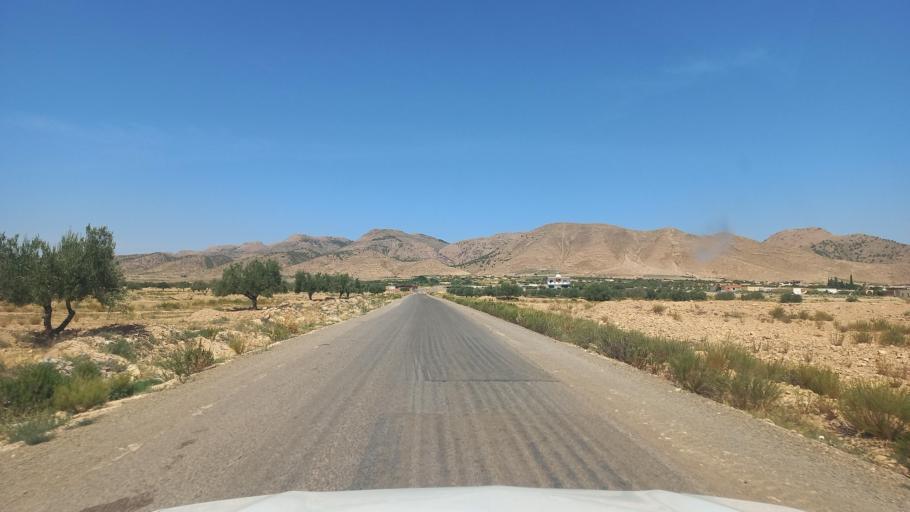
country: TN
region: Al Qasrayn
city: Sbiba
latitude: 35.4399
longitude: 9.0762
